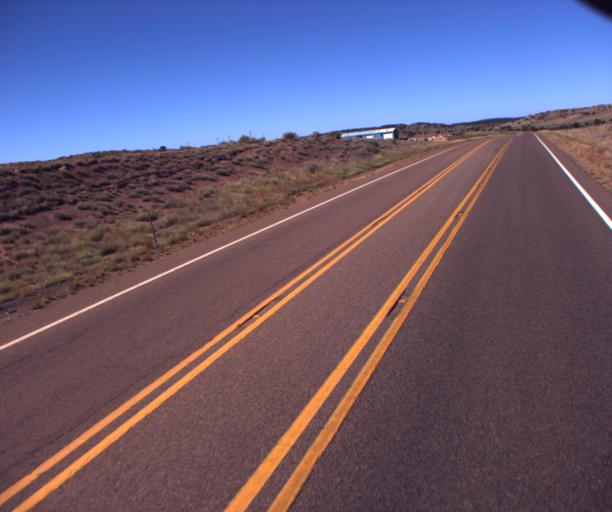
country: US
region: Arizona
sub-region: Navajo County
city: Snowflake
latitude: 34.5128
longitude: -110.1466
